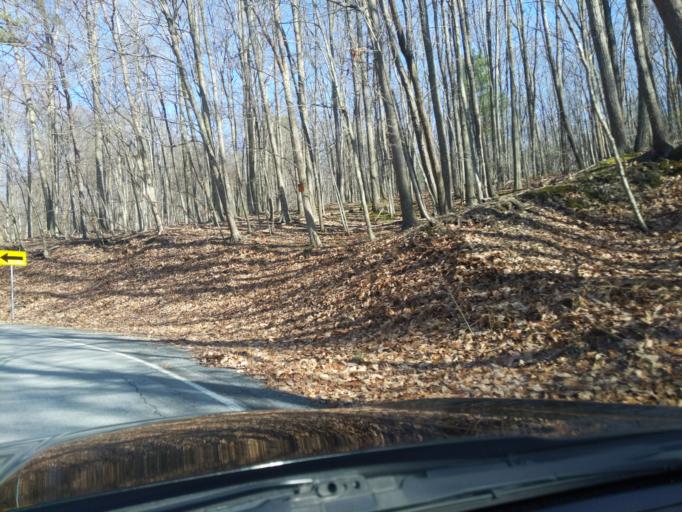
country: US
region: Pennsylvania
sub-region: Blair County
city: Tipton
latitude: 40.6231
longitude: -78.2746
